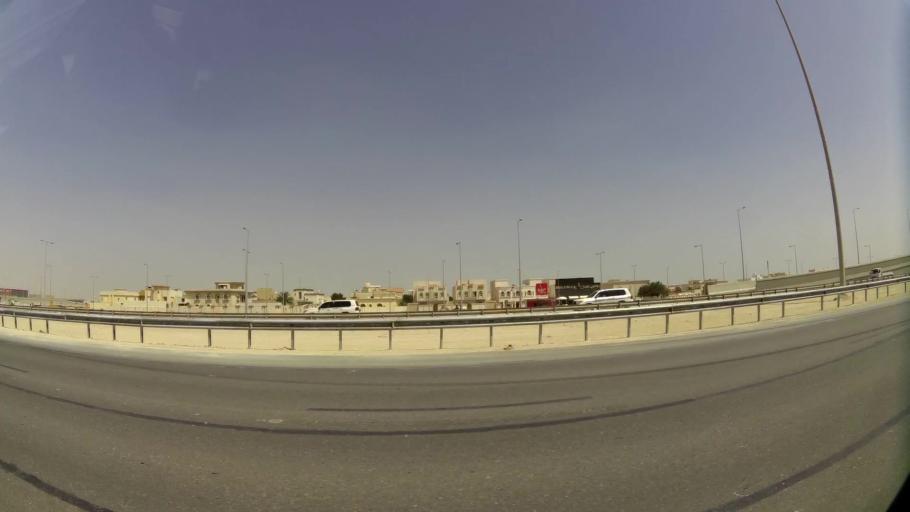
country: QA
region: Baladiyat Umm Salal
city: Umm Salal Muhammad
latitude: 25.3744
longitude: 51.4428
